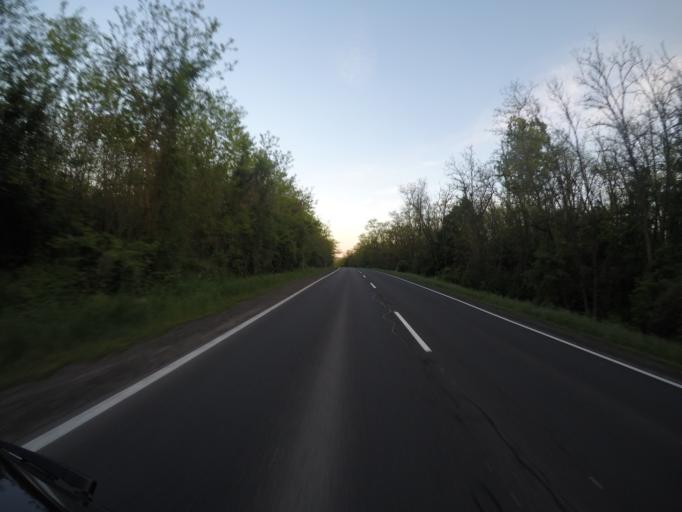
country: HU
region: Nograd
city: Retsag
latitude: 47.9512
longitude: 19.1450
